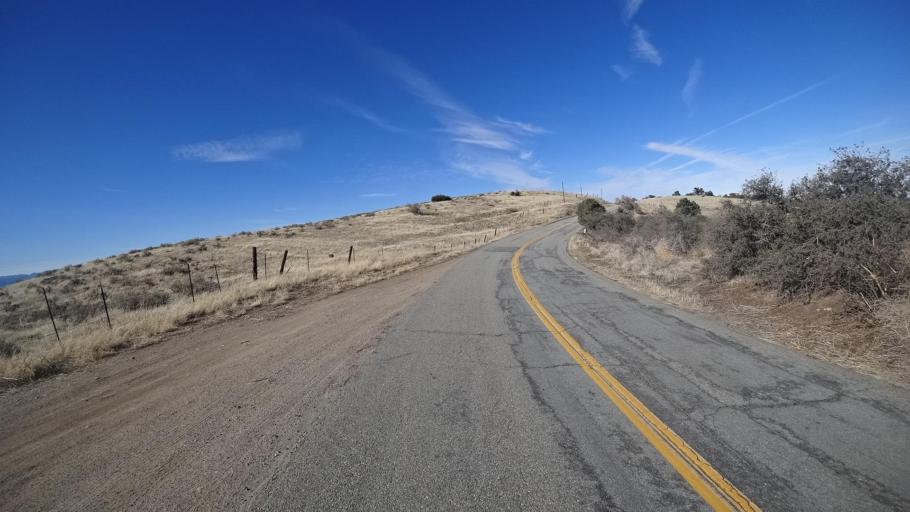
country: US
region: California
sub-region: Kern County
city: Pine Mountain Club
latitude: 34.8683
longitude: -119.3257
